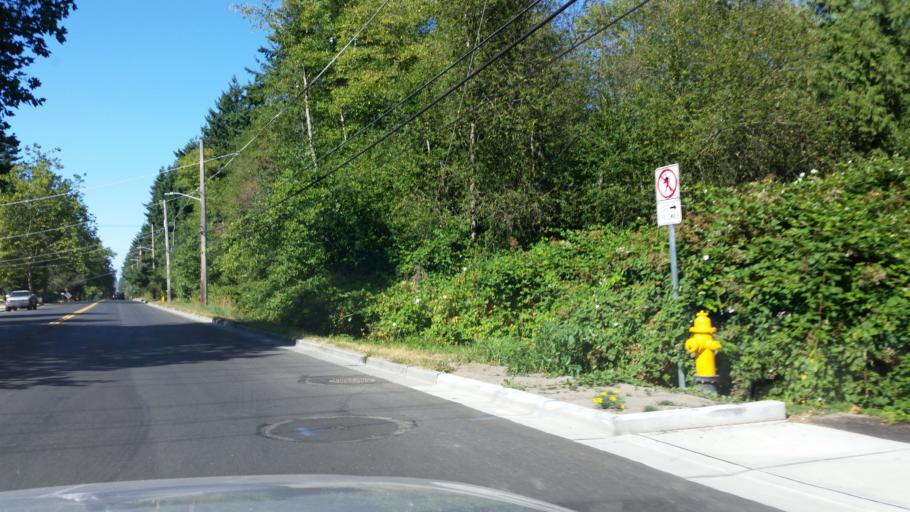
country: US
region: Washington
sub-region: King County
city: Shoreline
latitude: 47.7706
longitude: -122.3352
